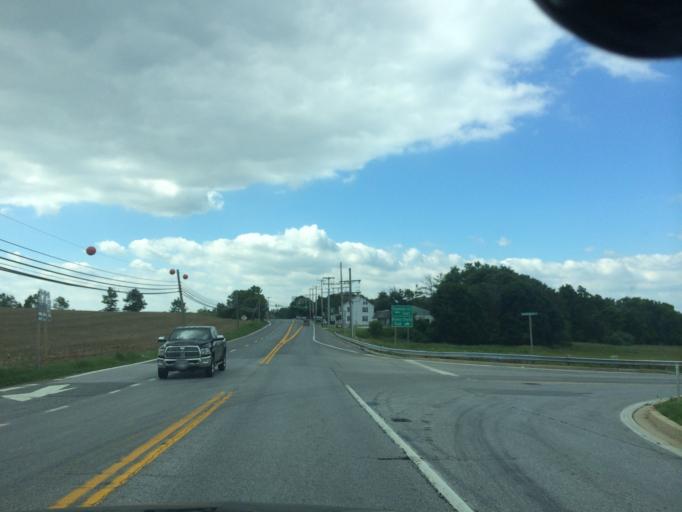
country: US
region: Maryland
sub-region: Carroll County
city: Westminster
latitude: 39.5990
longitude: -76.9990
